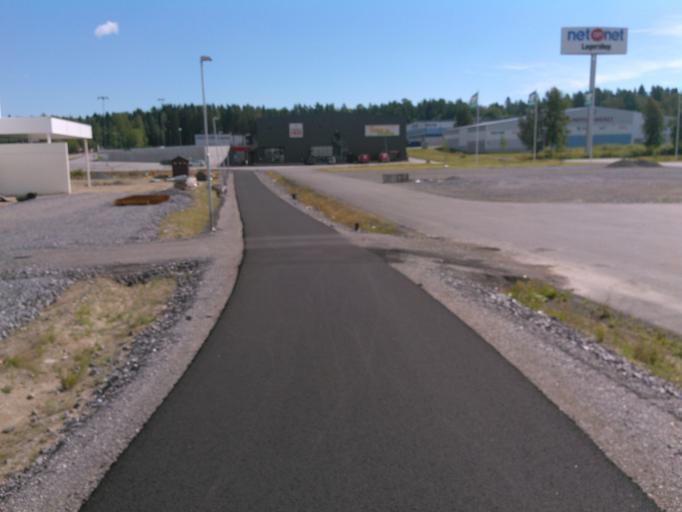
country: SE
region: Vaesterbotten
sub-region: Umea Kommun
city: Ersmark
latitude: 63.8500
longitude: 20.3189
